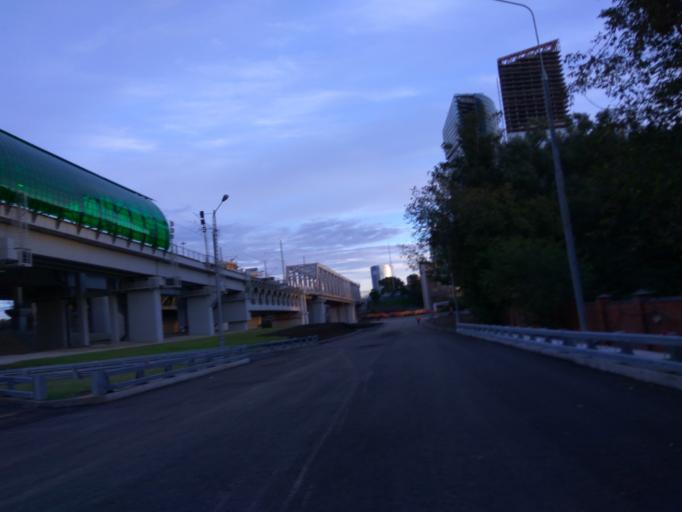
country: RU
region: Moskovskaya
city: Presnenskiy
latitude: 55.7468
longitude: 37.5316
